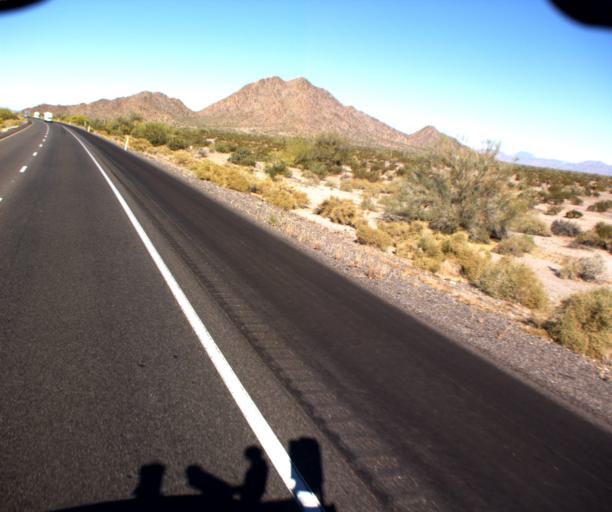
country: US
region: Arizona
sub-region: Maricopa County
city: Gila Bend
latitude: 32.9076
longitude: -112.5418
